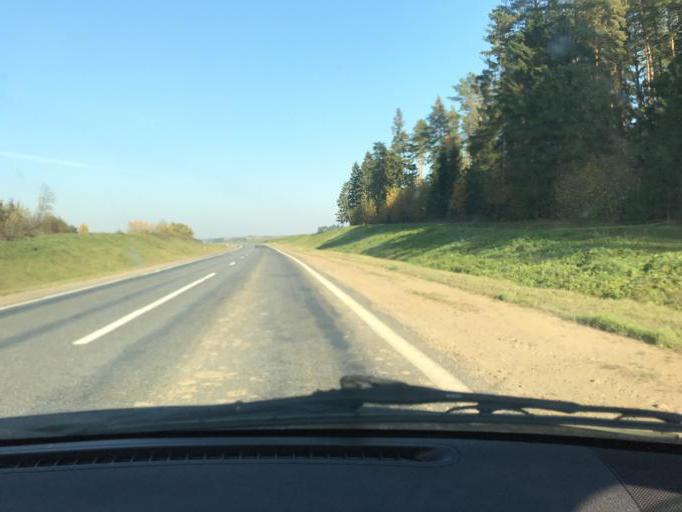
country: BY
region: Vitebsk
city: Orsha
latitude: 54.4157
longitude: 30.4664
